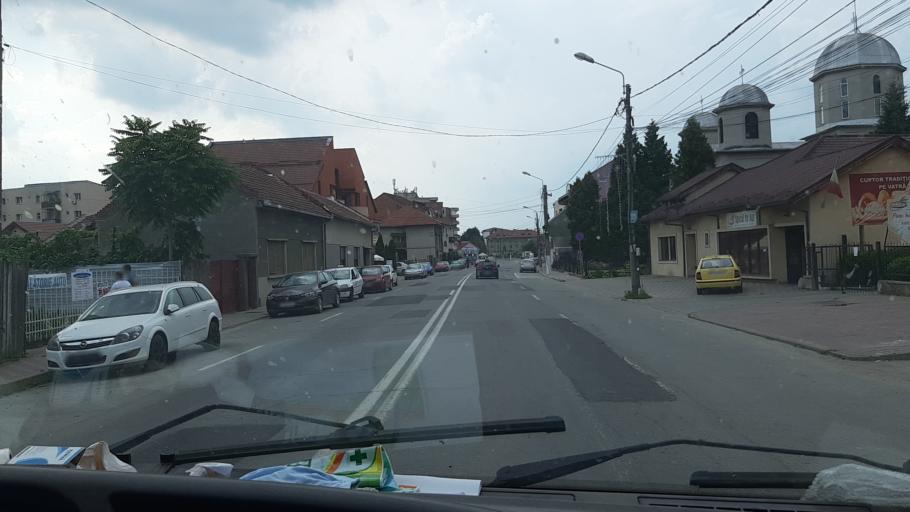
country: RO
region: Timis
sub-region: Municipiul Lugoj
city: Lugoj
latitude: 45.6952
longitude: 21.9013
